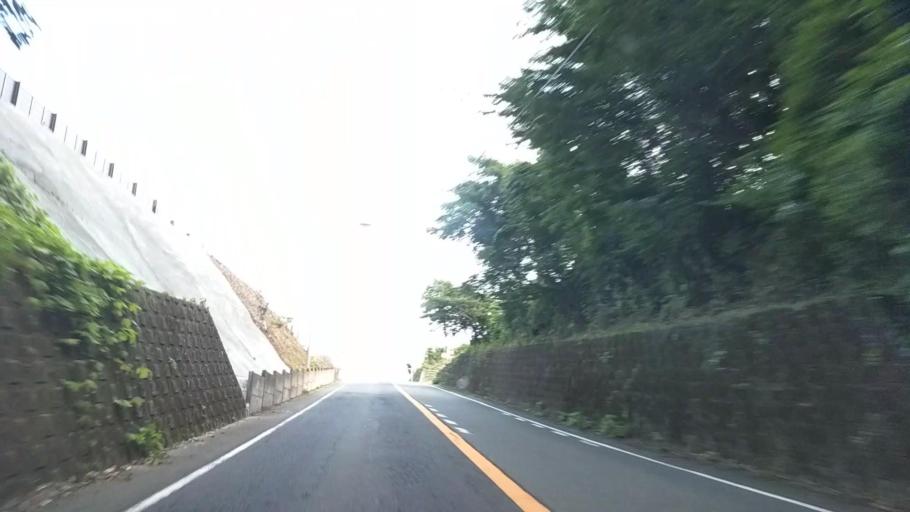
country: JP
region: Tokyo
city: Hachioji
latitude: 35.5764
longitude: 139.2624
